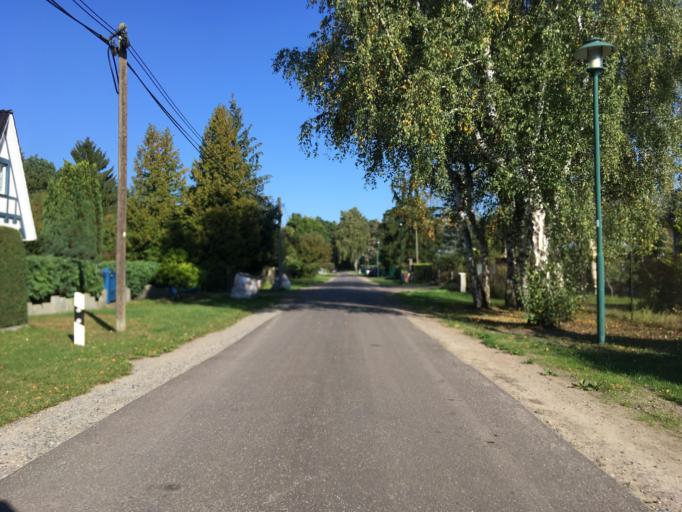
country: DE
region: Berlin
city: Buch
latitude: 52.6710
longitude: 13.5201
